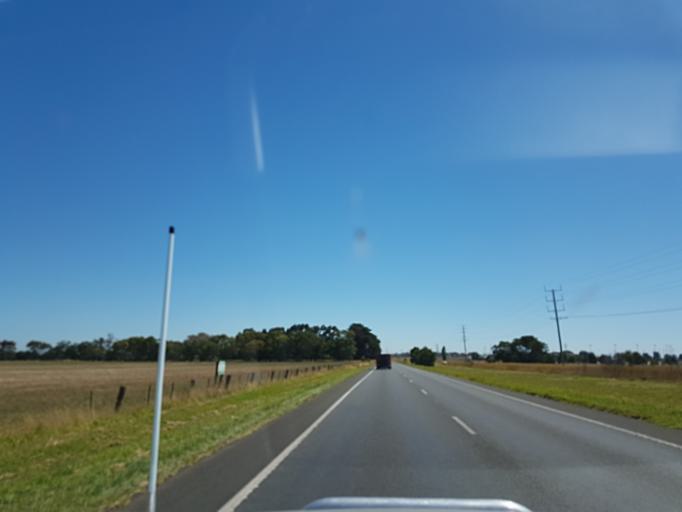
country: AU
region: Victoria
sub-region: Warrnambool
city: Allansford
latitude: -38.2277
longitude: 142.9541
